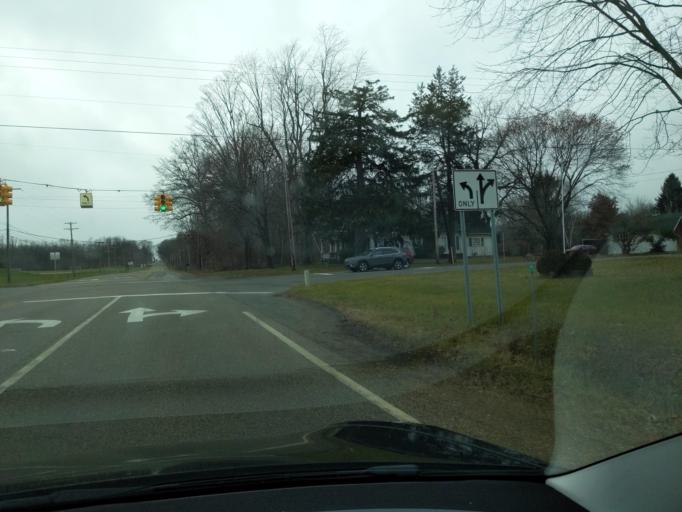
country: US
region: Michigan
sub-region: Jackson County
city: Spring Arbor
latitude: 42.2525
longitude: -84.5368
